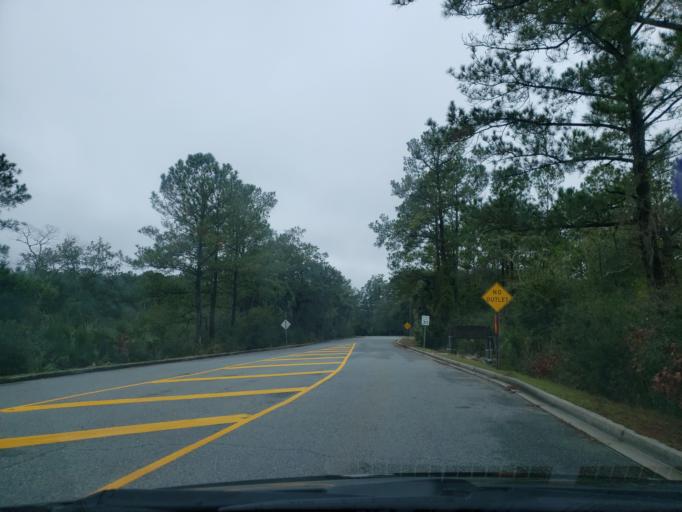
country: US
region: Georgia
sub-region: Chatham County
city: Georgetown
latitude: 31.9823
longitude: -81.1781
